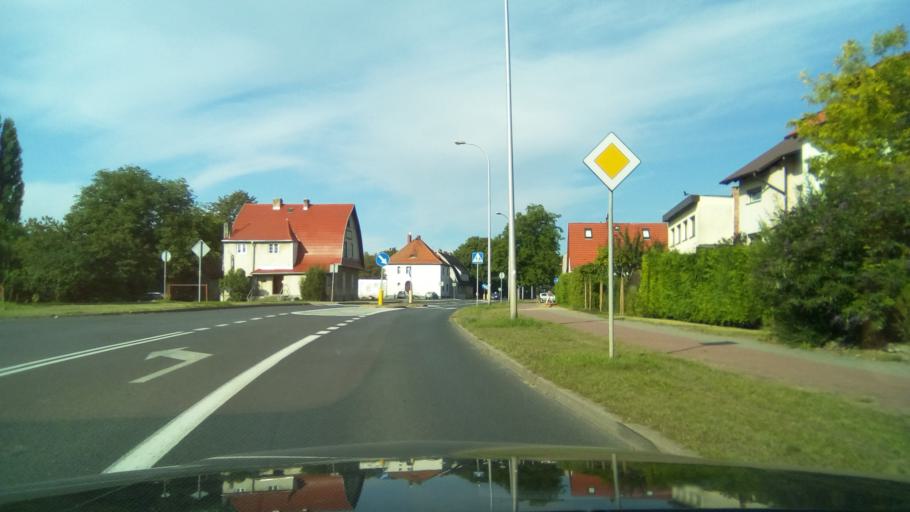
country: PL
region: Greater Poland Voivodeship
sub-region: Powiat pilski
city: Pila
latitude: 53.1427
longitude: 16.7182
